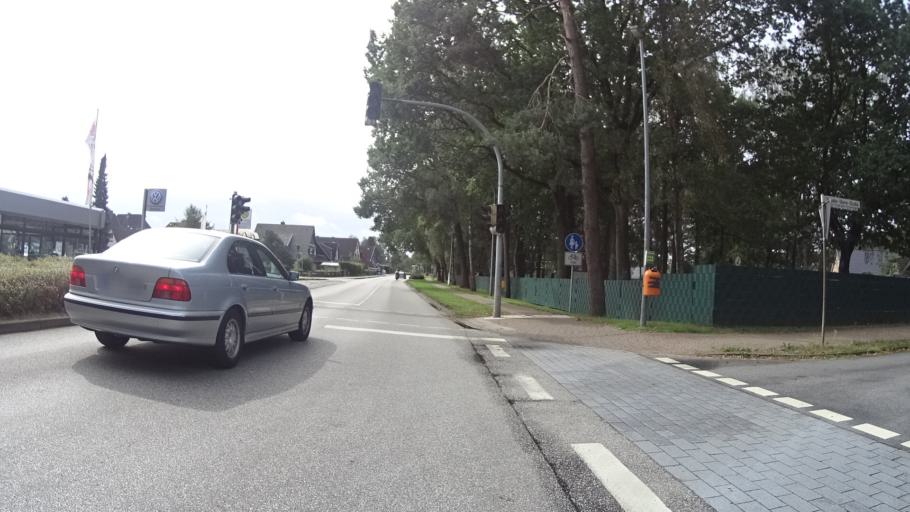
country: DE
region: Schleswig-Holstein
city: Henstedt-Ulzburg
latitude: 53.7597
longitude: 9.9968
